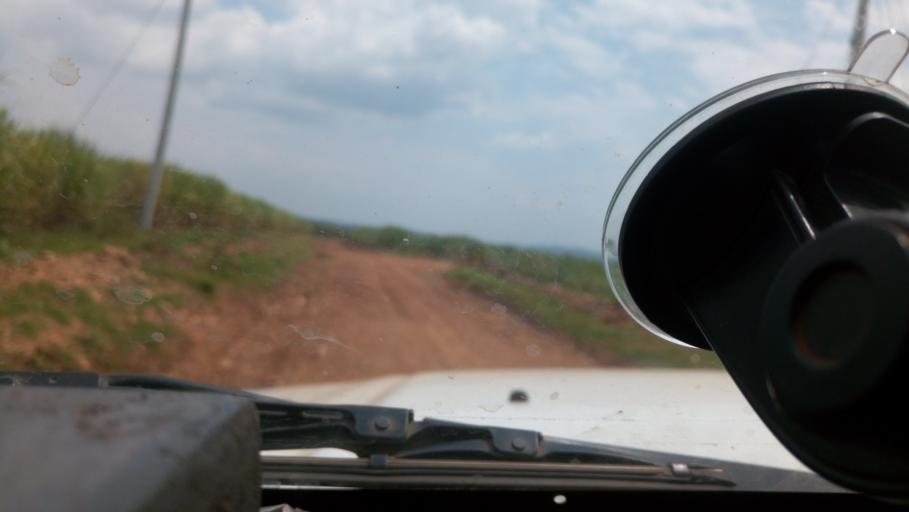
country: KE
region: Migori
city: Migori
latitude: -0.9211
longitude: 34.5241
